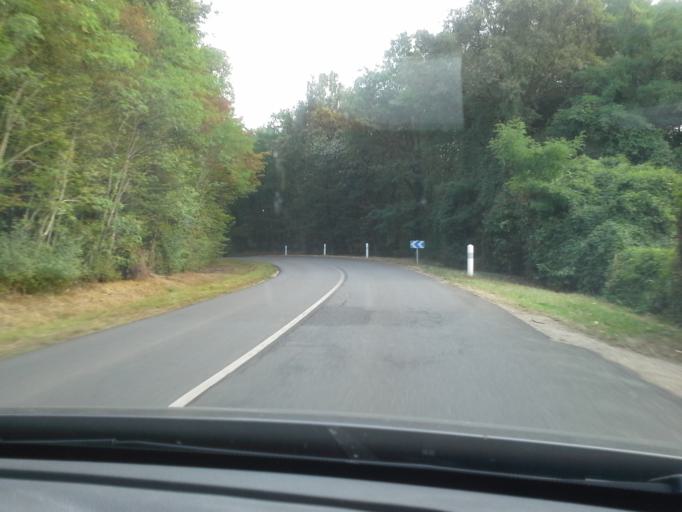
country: FR
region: Centre
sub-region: Departement du Loir-et-Cher
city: Saint-Sulpice-de-Pommeray
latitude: 47.5853
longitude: 1.2037
